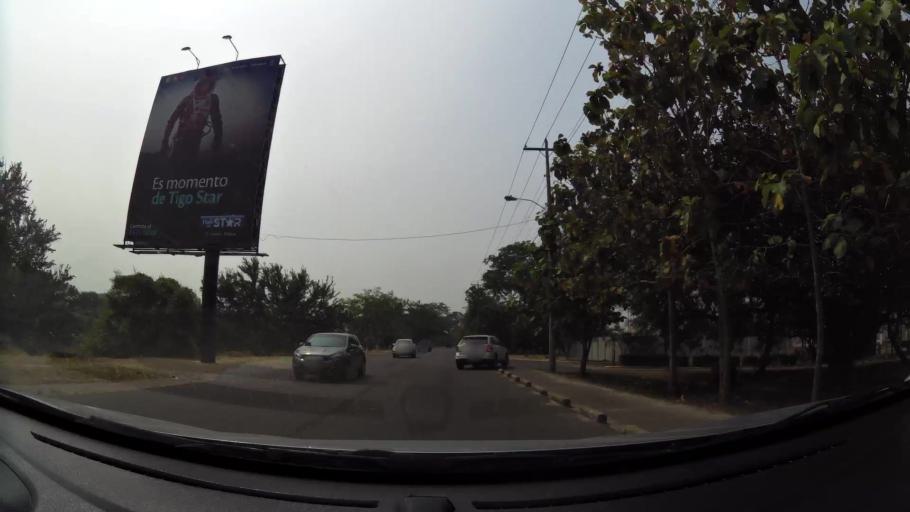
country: HN
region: Cortes
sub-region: San Pedro Sula
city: Pena Blanca
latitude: 15.5552
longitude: -88.0139
